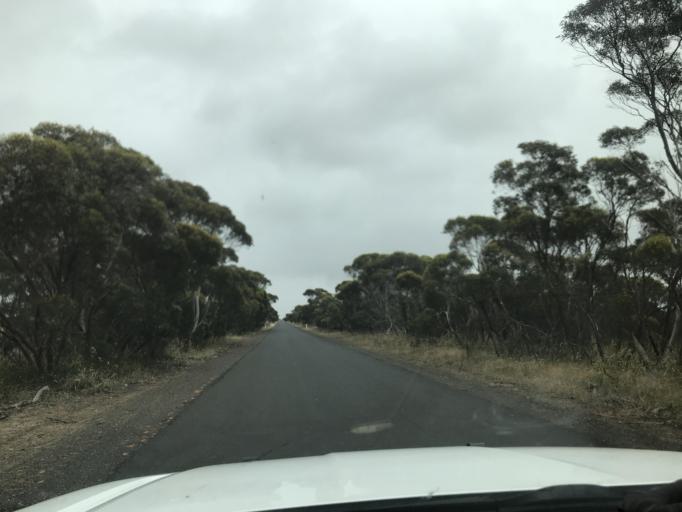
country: AU
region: South Australia
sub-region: Tatiara
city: Bordertown
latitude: -36.1190
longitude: 141.0521
